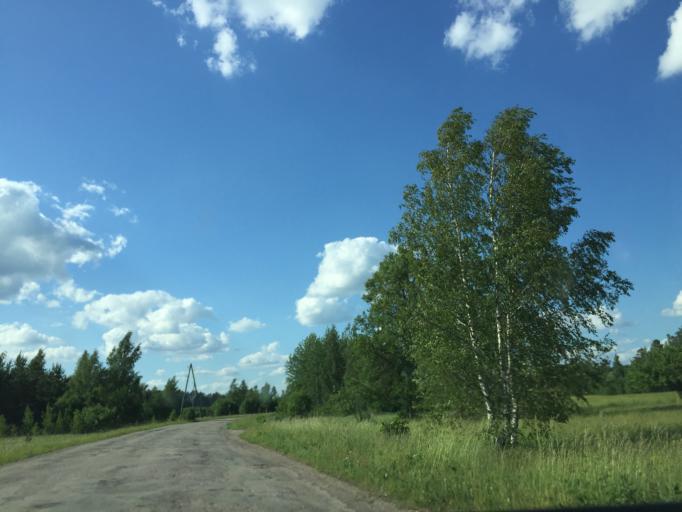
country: LV
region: Jaunpils
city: Jaunpils
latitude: 56.8860
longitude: 22.9838
